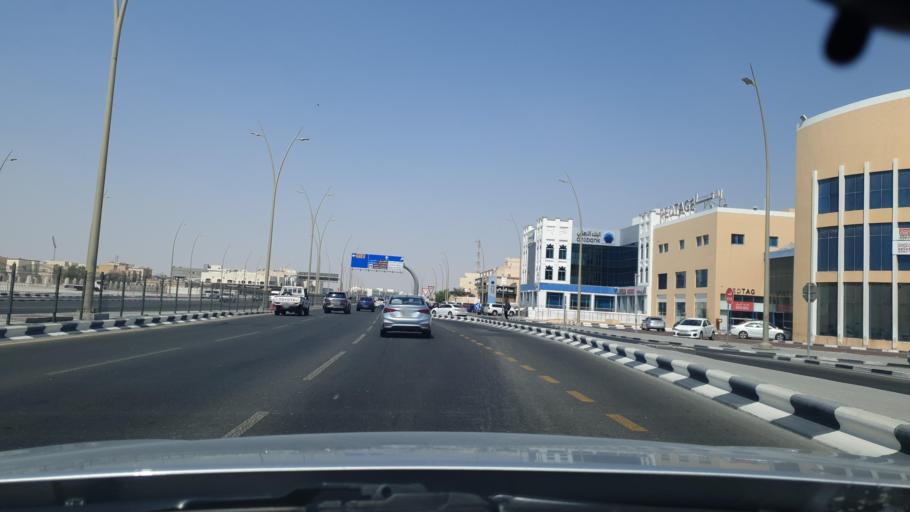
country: QA
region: Al Khawr
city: Al Khawr
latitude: 25.6761
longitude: 51.5002
